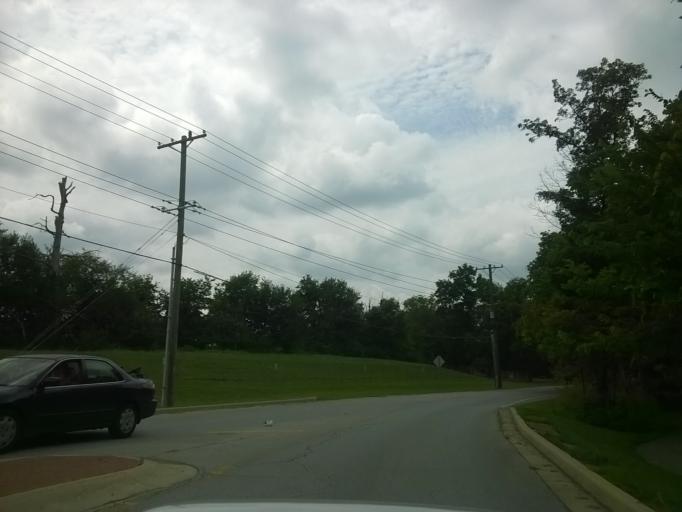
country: US
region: Indiana
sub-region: Hamilton County
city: Carmel
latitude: 39.9415
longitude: -86.0888
